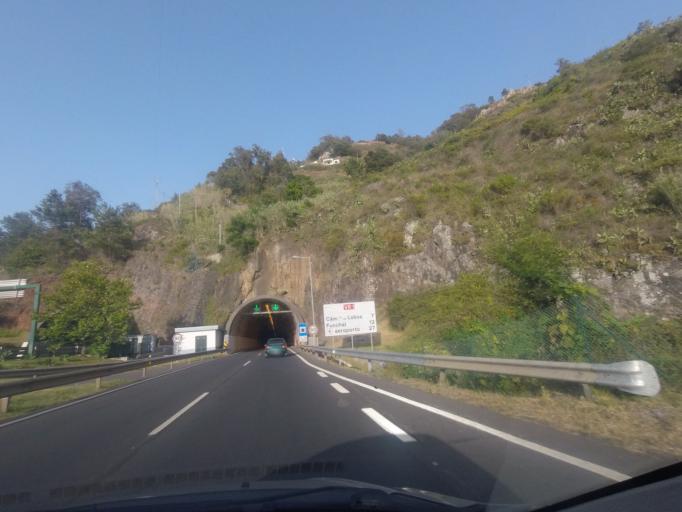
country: PT
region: Madeira
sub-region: Ribeira Brava
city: Campanario
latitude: 32.6589
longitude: -17.0111
